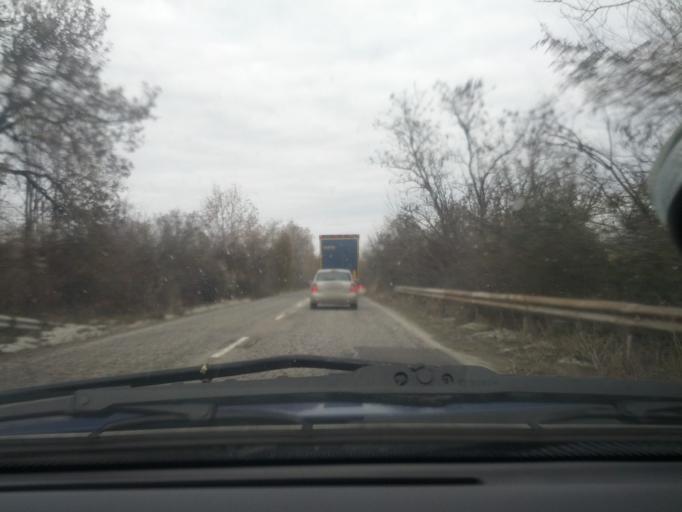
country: BG
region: Vratsa
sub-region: Obshtina Borovan
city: Borovan
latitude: 43.3191
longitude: 23.6818
